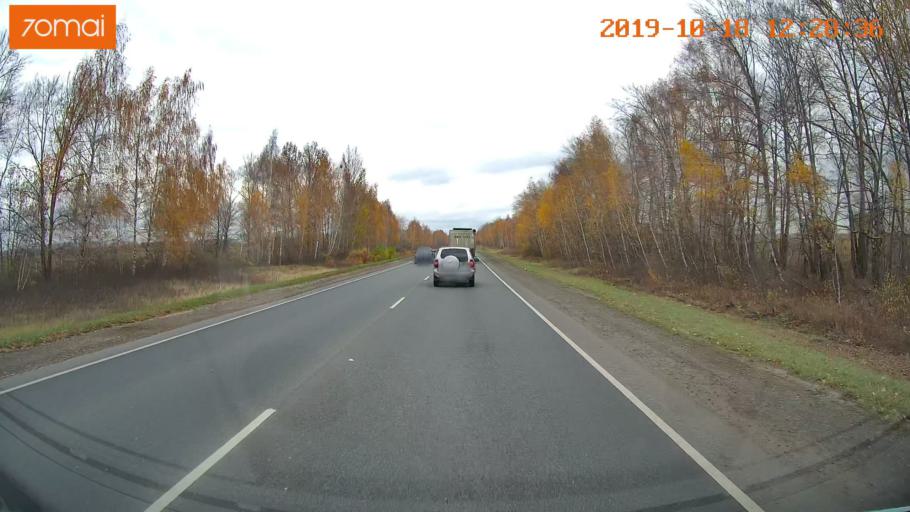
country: RU
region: Rjazan
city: Ryazan'
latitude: 54.5731
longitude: 39.5712
